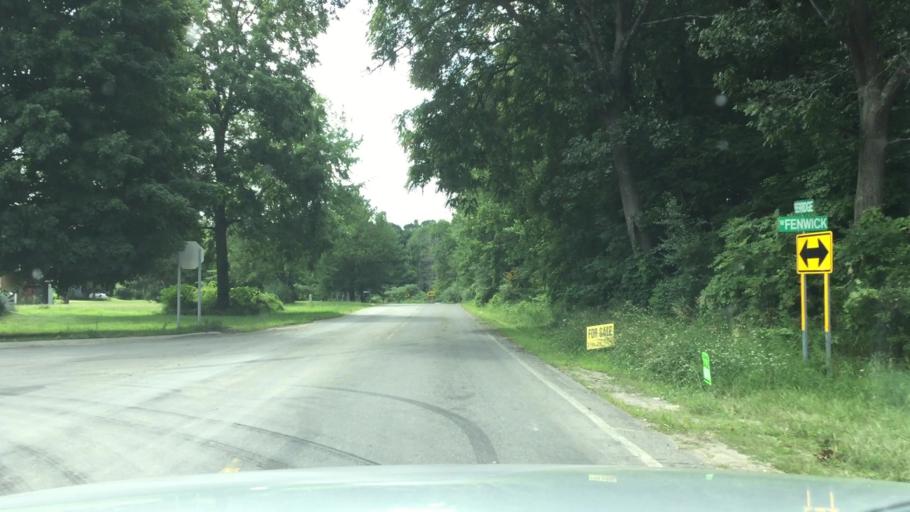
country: US
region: Michigan
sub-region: Montcalm County
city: Greenville
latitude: 43.1488
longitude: -85.2136
